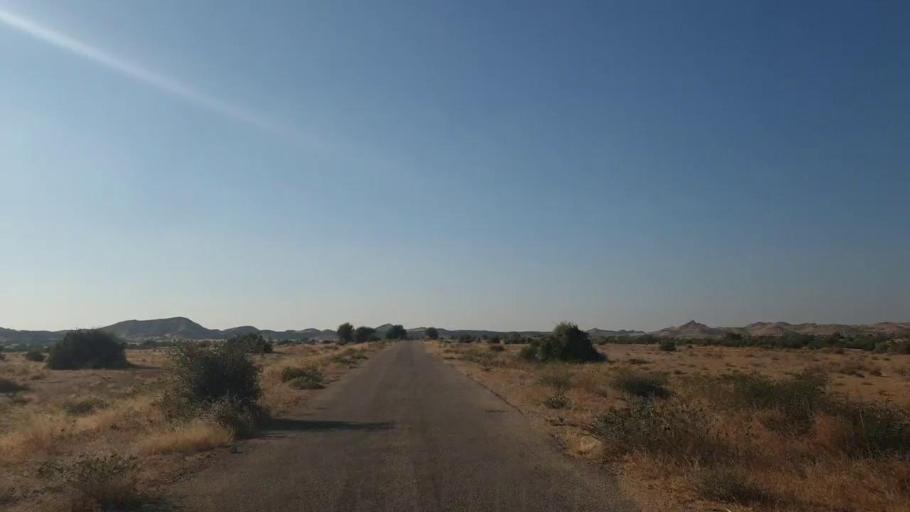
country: PK
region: Sindh
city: Malir Cantonment
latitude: 25.3915
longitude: 67.5027
